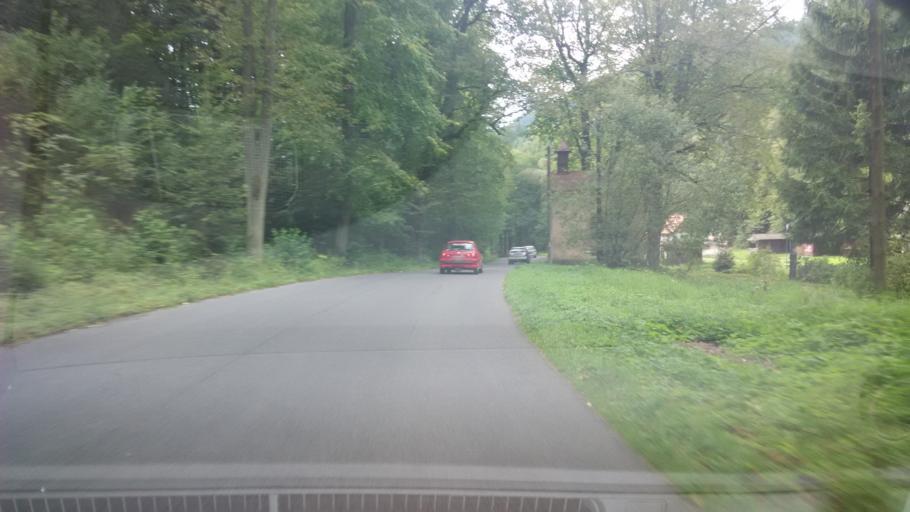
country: SK
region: Banskobystricky
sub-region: Okres Ziar nad Hronom
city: Kremnica
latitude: 48.7066
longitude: 18.9418
